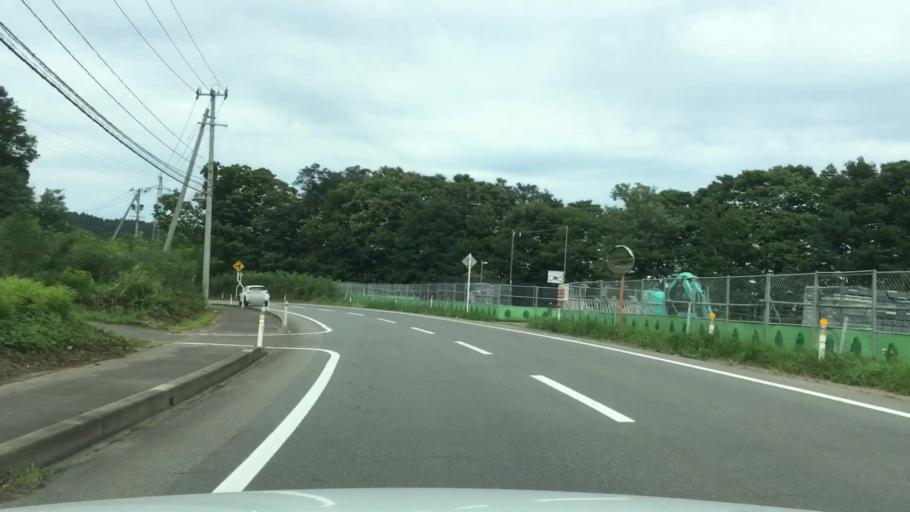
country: JP
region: Aomori
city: Shimokizukuri
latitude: 40.7665
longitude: 140.2243
